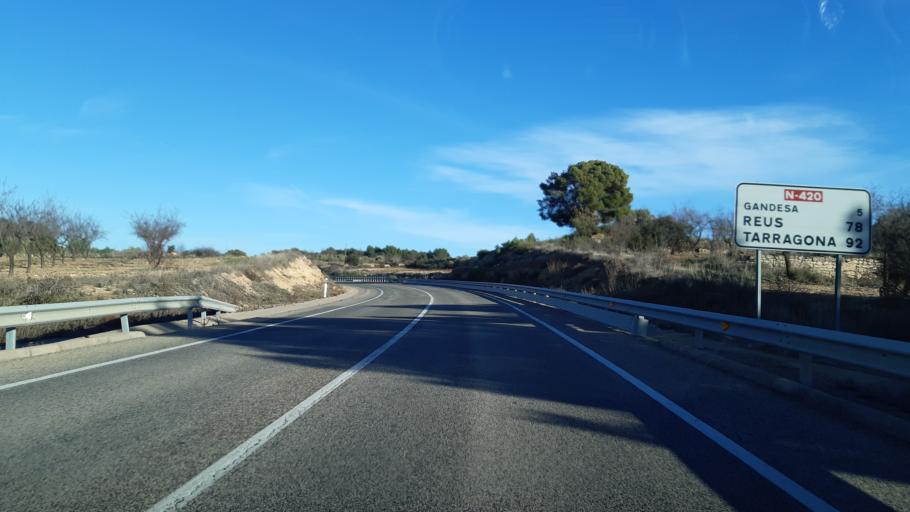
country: ES
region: Catalonia
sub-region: Provincia de Tarragona
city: Bot
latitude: 41.0501
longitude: 0.3828
